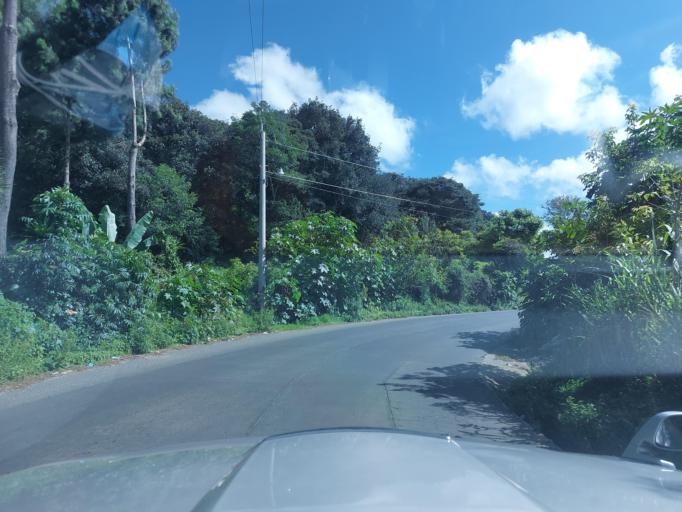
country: GT
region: Chimaltenango
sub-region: Municipio de Zaragoza
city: Zaragoza
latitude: 14.6513
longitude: -90.8979
